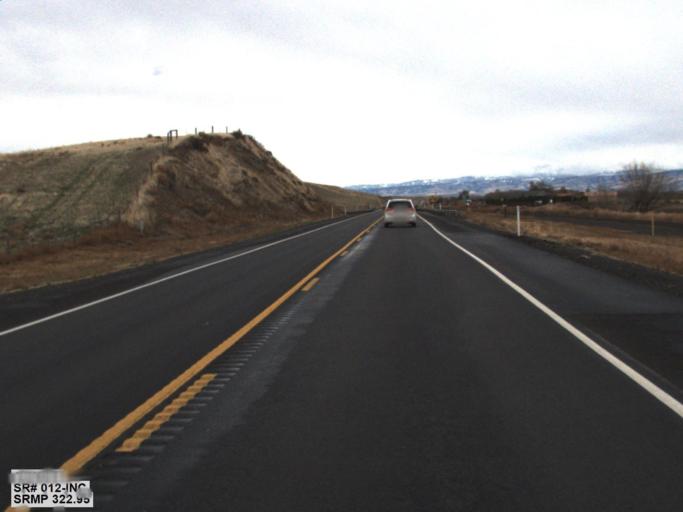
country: US
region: Washington
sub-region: Walla Walla County
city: Garrett
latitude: 46.0529
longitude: -118.6142
